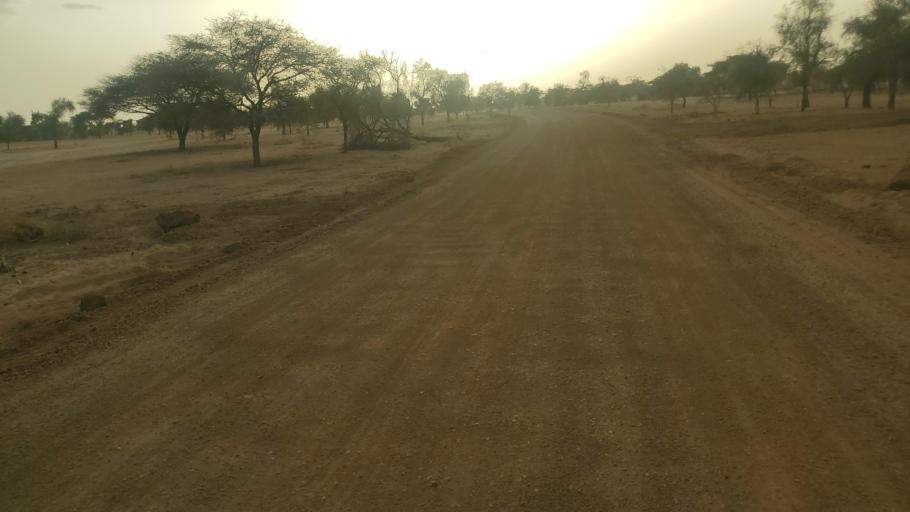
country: SN
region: Louga
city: Dara
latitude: 15.3728
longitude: -15.5833
